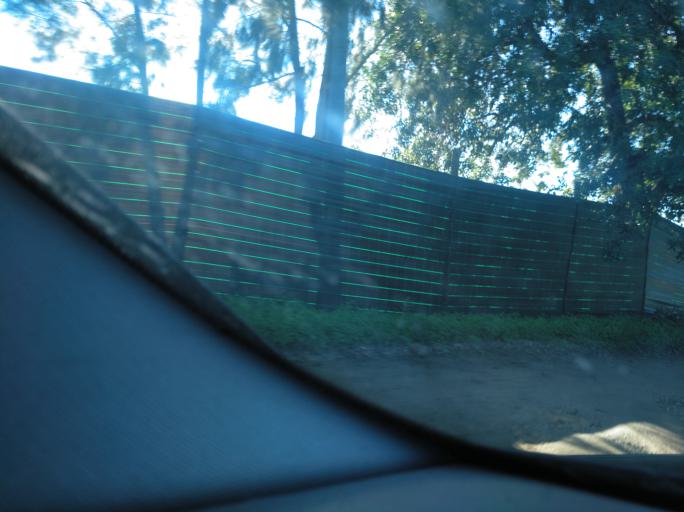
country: PT
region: Faro
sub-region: Tavira
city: Tavira
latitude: 37.1560
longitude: -7.5811
